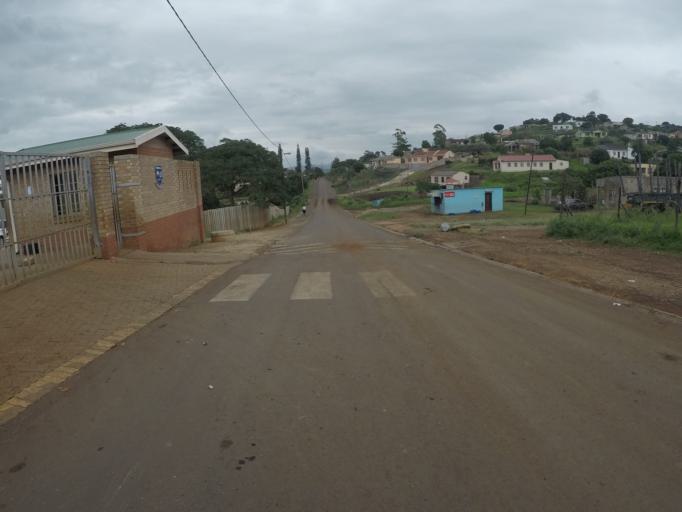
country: ZA
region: KwaZulu-Natal
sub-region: uThungulu District Municipality
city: Empangeni
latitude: -28.7712
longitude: 31.8585
